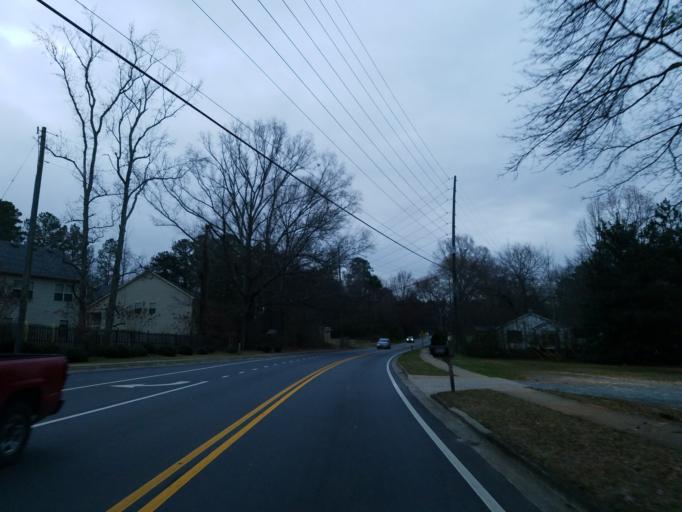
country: US
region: Georgia
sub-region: Cobb County
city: Acworth
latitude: 34.0433
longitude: -84.6551
